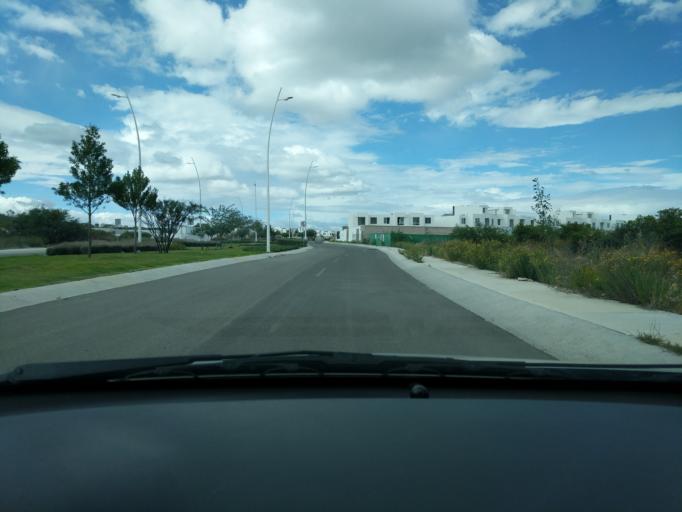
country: MX
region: Queretaro
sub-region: El Marques
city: La Pradera
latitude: 20.6601
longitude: -100.3177
